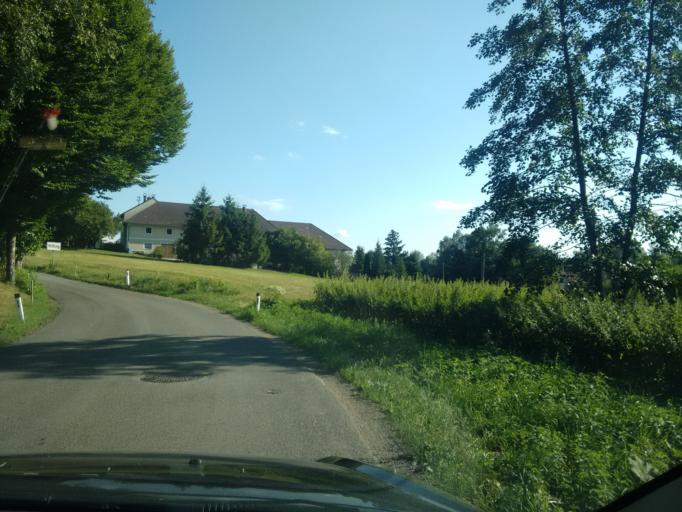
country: AT
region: Upper Austria
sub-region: Wels-Land
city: Buchkirchen
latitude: 48.2326
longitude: 13.9720
